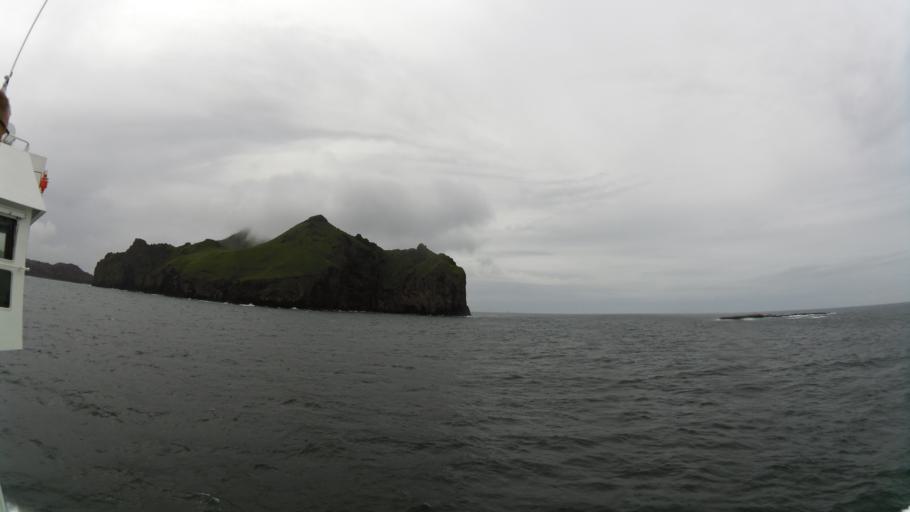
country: IS
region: South
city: Vestmannaeyjar
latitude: 63.4549
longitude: -20.2277
